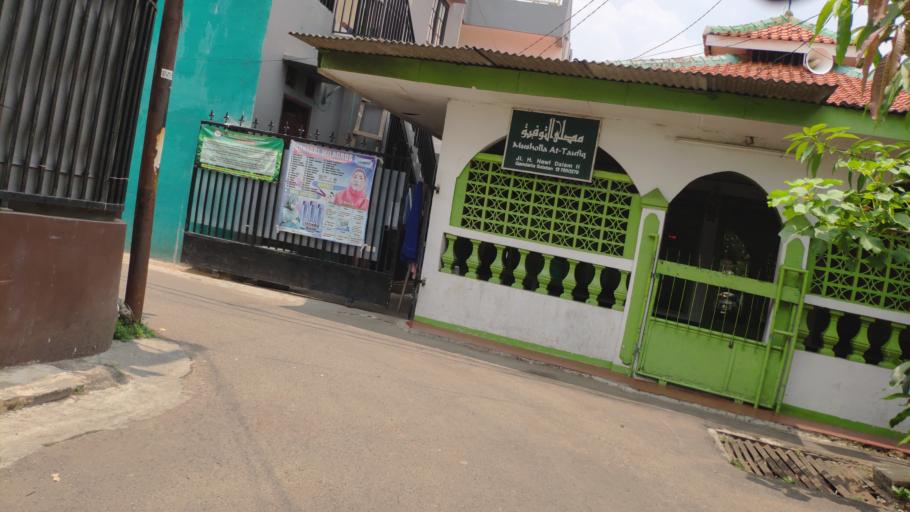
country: ID
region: Jakarta Raya
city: Jakarta
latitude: -6.2650
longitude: 106.7929
